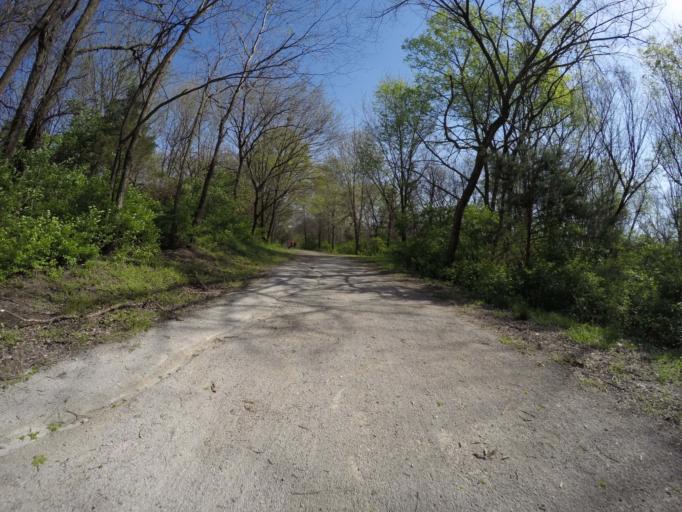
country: US
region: Missouri
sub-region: Jackson County
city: Grandview
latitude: 38.9000
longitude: -94.4895
